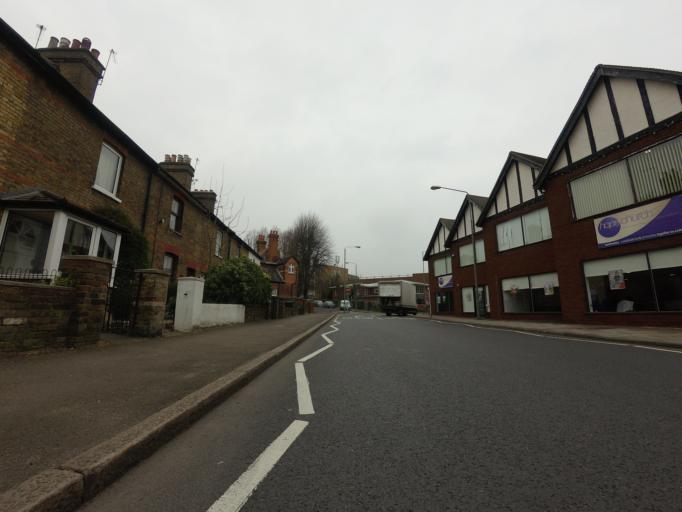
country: GB
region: England
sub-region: Greater London
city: Orpington
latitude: 51.3810
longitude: 0.1024
